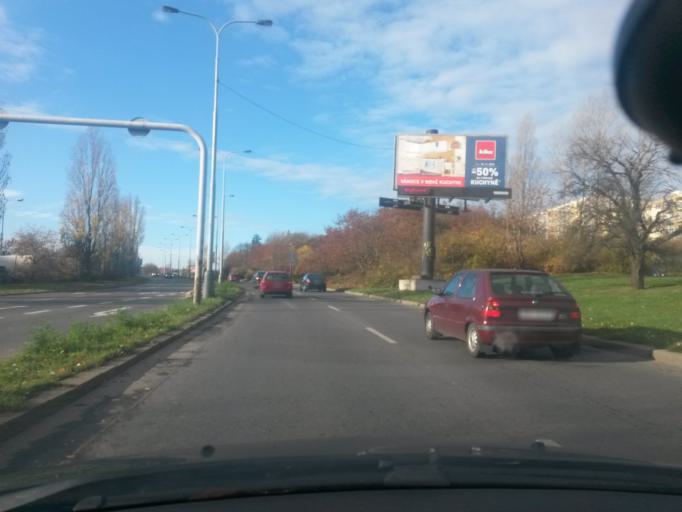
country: CZ
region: Central Bohemia
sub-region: Okres Praha-Zapad
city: Pruhonice
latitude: 50.0252
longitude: 14.5143
